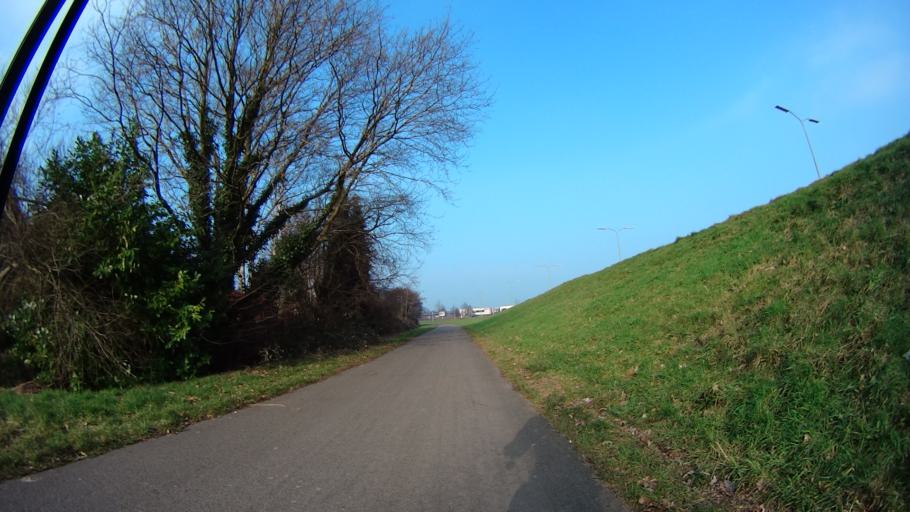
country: NL
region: Drenthe
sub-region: Gemeente Emmen
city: Emmen
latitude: 52.7686
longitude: 6.8965
